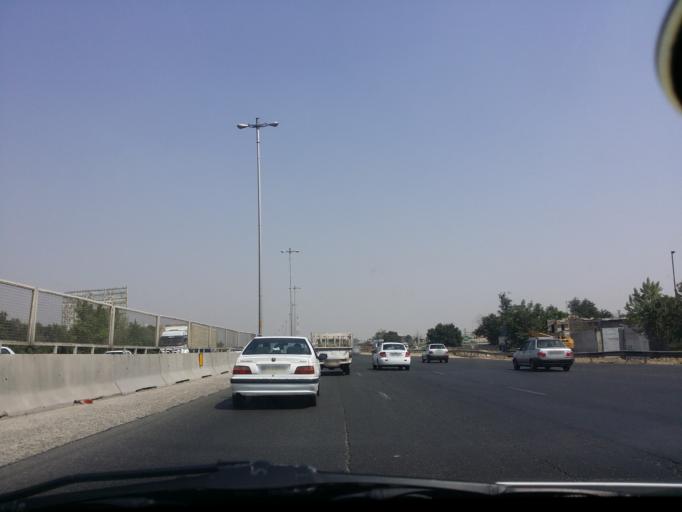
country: IR
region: Alborz
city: Karaj
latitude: 35.7992
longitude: 50.9726
